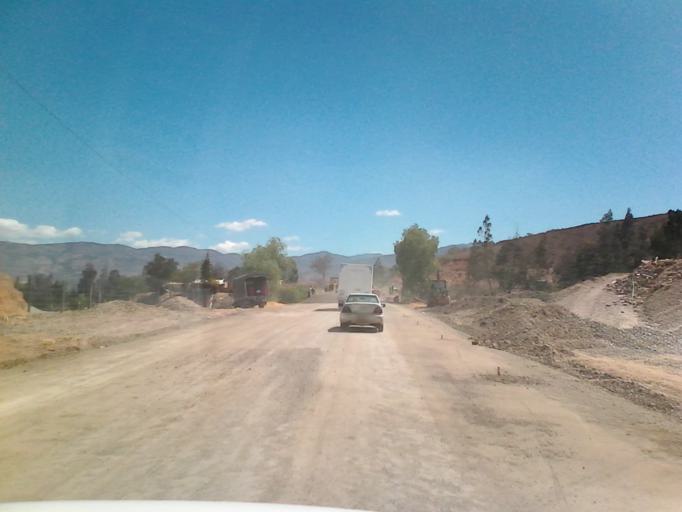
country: CO
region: Boyaca
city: Villa de Leiva
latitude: 5.6156
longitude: -73.5667
